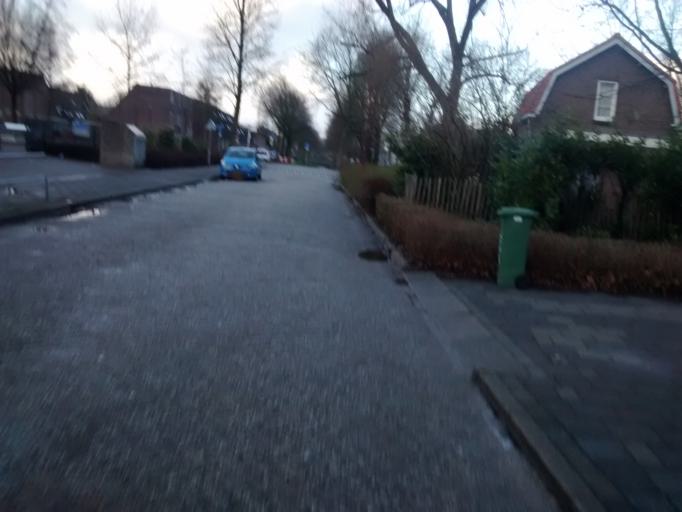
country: NL
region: Utrecht
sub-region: Gemeente Vianen
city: Vianen
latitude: 52.0110
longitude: 5.0914
